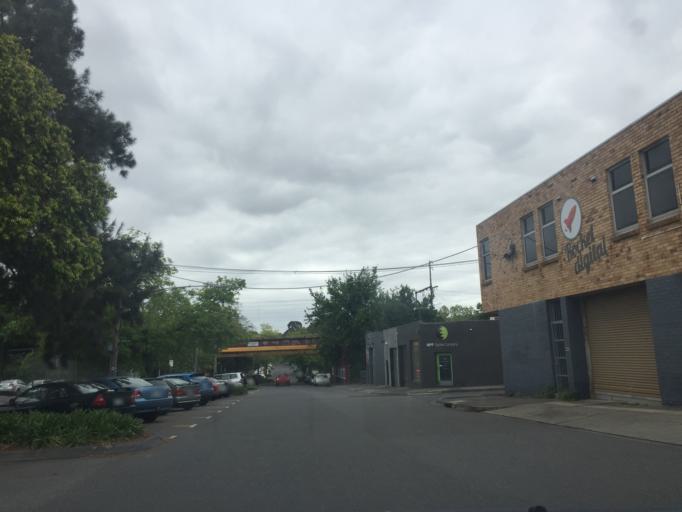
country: AU
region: Victoria
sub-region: Boroondara
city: Hawthorn East
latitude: -37.8231
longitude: 145.0423
